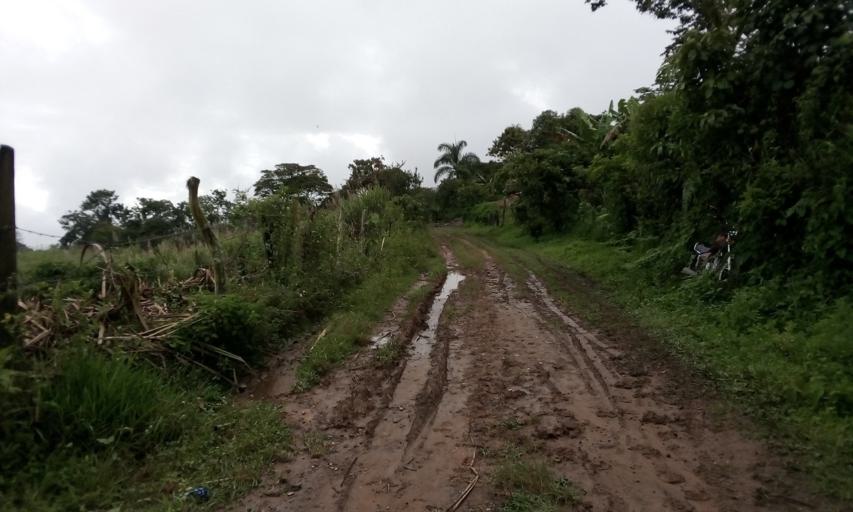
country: CO
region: Boyaca
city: Santana
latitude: 5.9997
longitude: -73.4979
